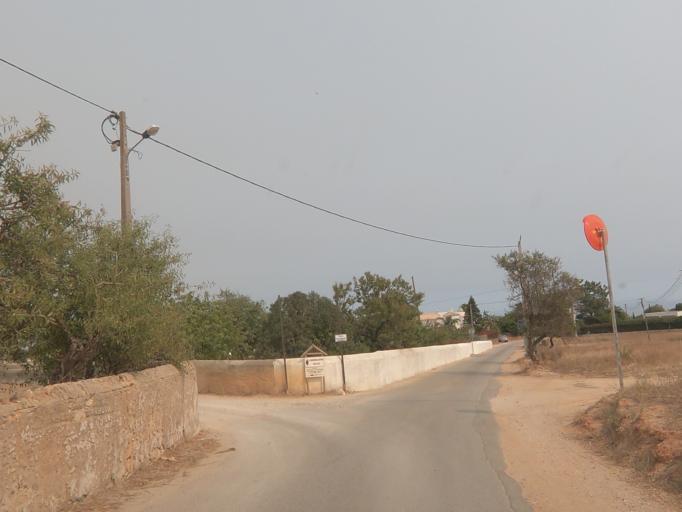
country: PT
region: Faro
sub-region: Lagoa
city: Carvoeiro
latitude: 37.0990
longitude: -8.4118
